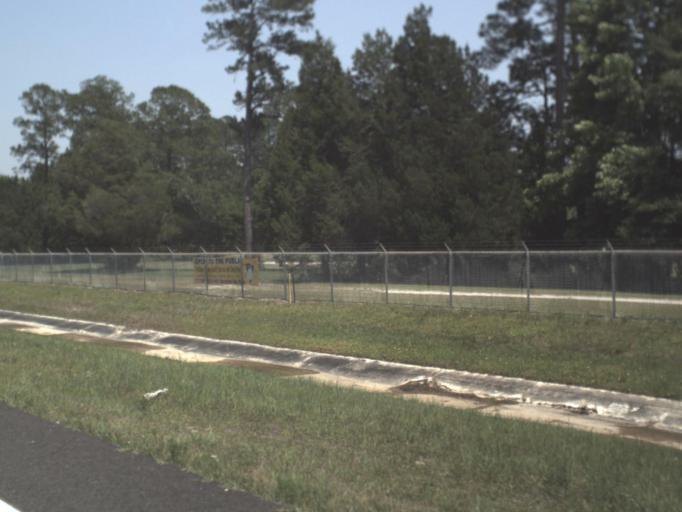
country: US
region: Florida
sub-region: Duval County
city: Baldwin
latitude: 30.2437
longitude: -81.8957
